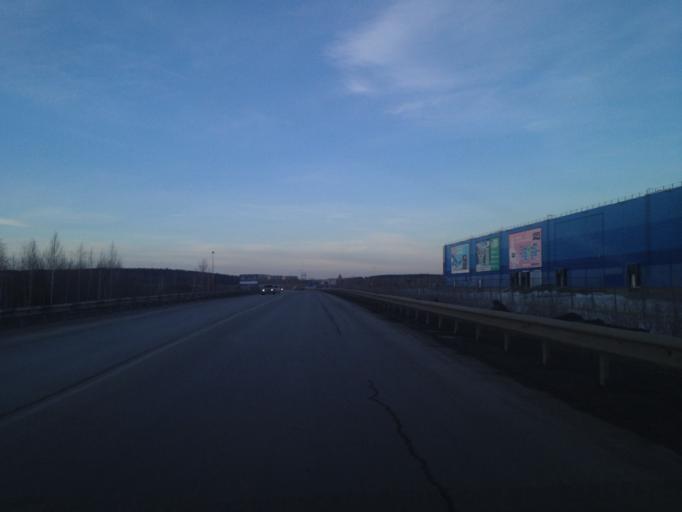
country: RU
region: Sverdlovsk
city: Istok
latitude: 56.7625
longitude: 60.7412
